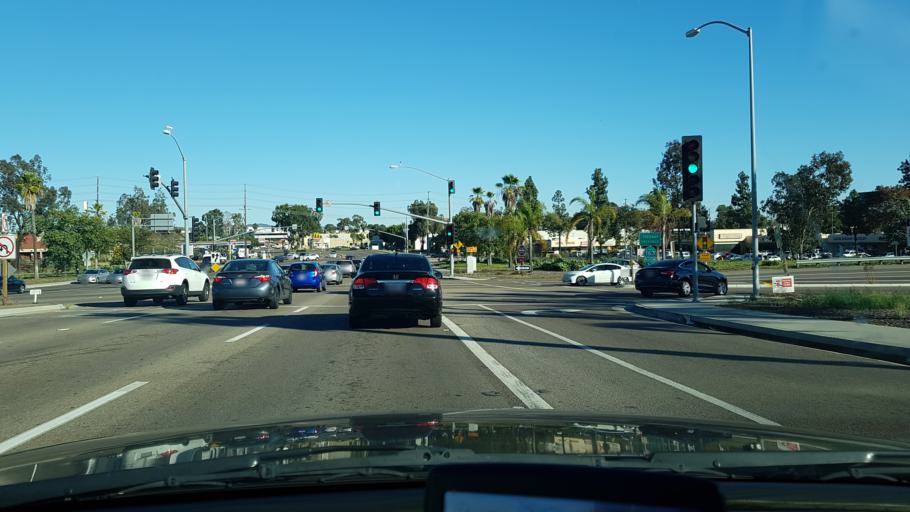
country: US
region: California
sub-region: San Diego County
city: San Diego
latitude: 32.8320
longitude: -117.1402
